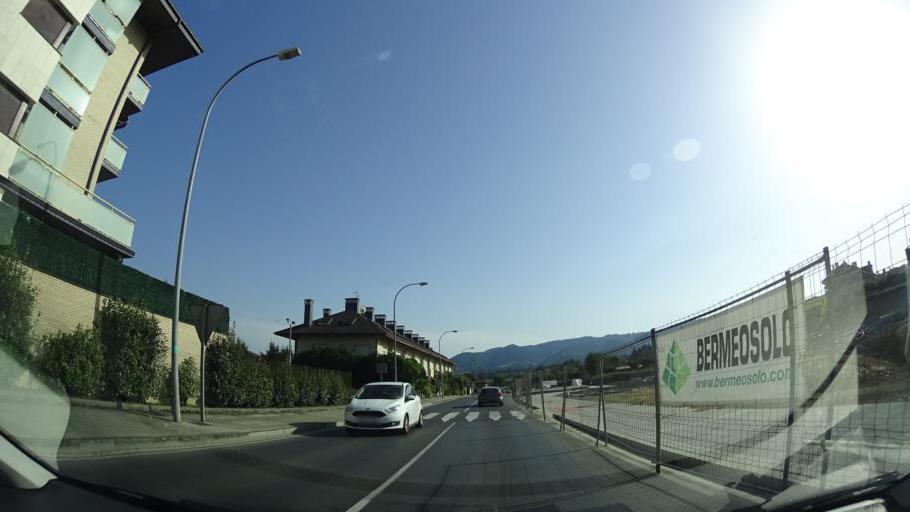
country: ES
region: Basque Country
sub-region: Bizkaia
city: Gernika-Lumo
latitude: 43.3050
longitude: -2.6821
